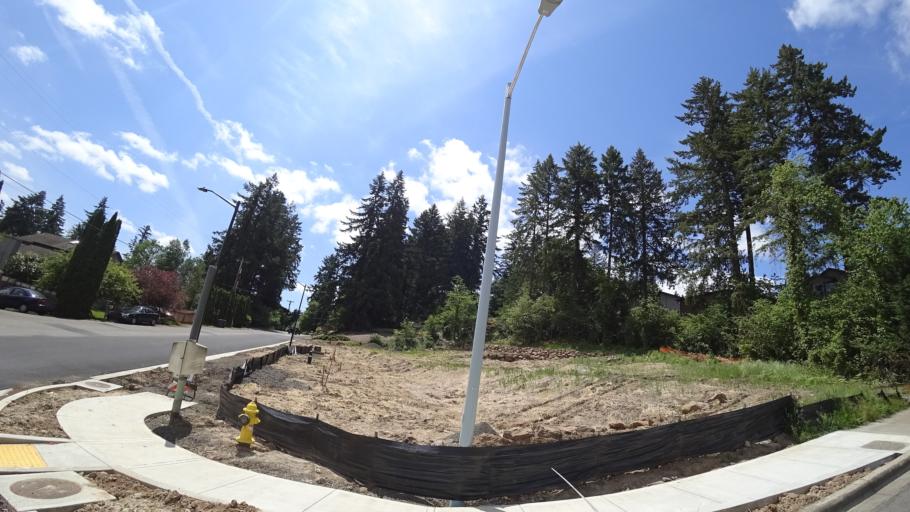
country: US
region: Oregon
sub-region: Washington County
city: King City
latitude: 45.4277
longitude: -122.8125
